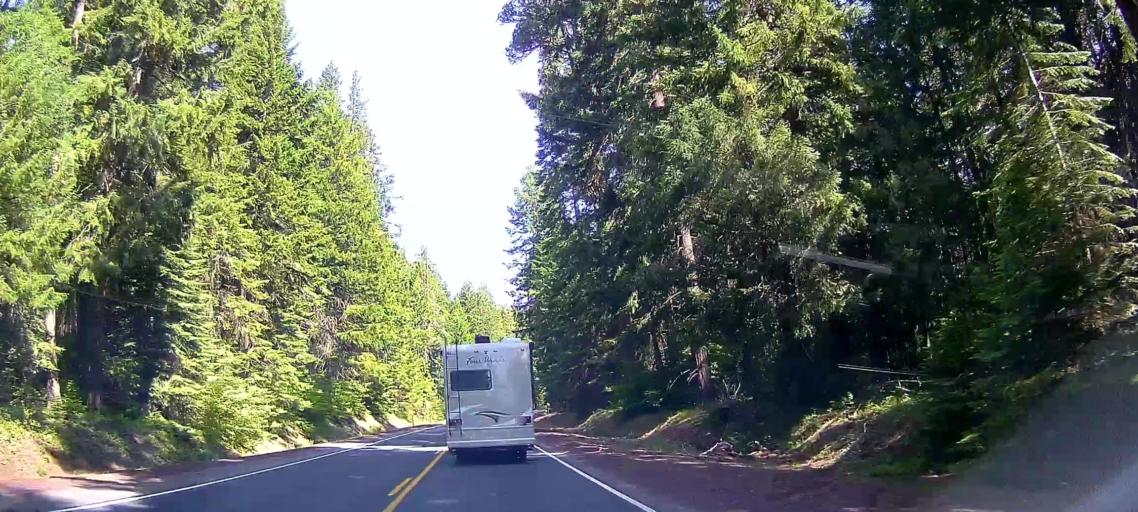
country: US
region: Oregon
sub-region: Jefferson County
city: Warm Springs
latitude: 45.0824
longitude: -121.5424
